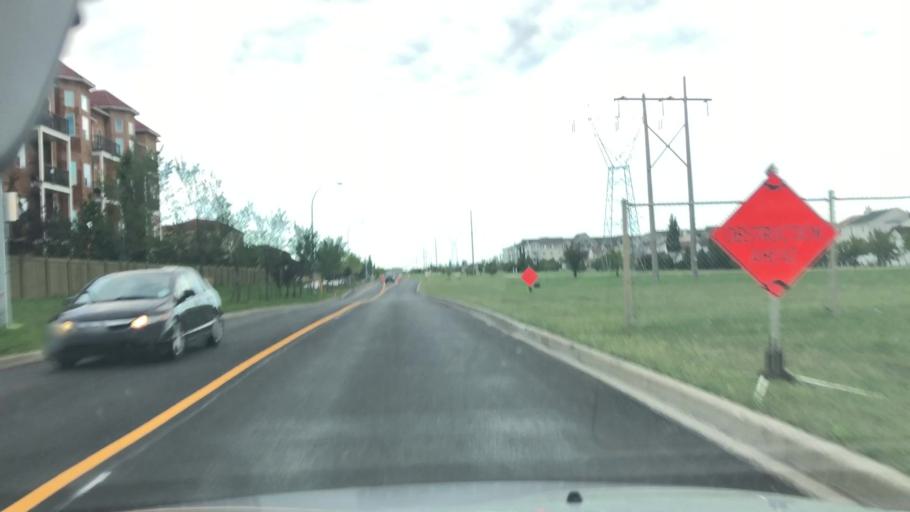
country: CA
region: Alberta
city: St. Albert
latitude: 53.6146
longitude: -113.5652
